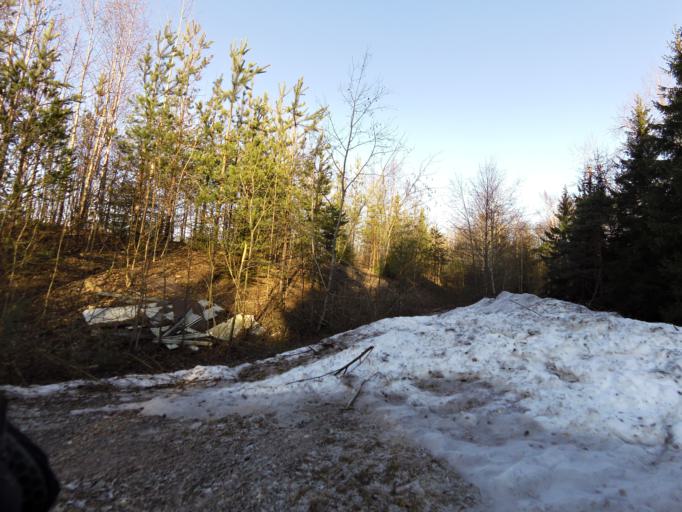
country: SE
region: Gaevleborg
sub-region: Gavle Kommun
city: Gavle
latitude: 60.6864
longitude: 17.2379
